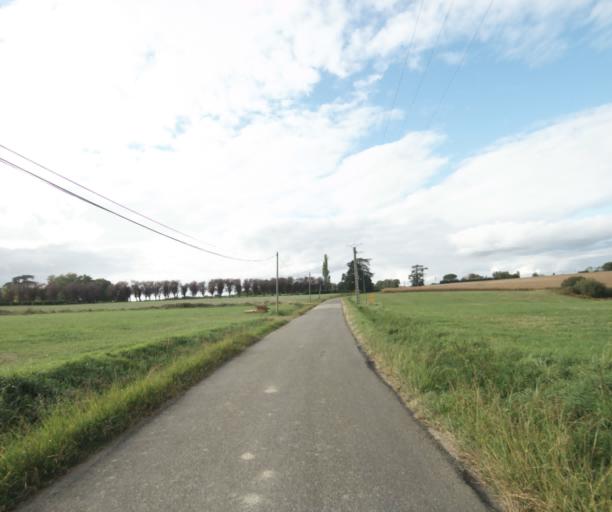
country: FR
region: Midi-Pyrenees
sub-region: Departement du Gers
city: Eauze
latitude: 43.8688
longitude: 0.0928
